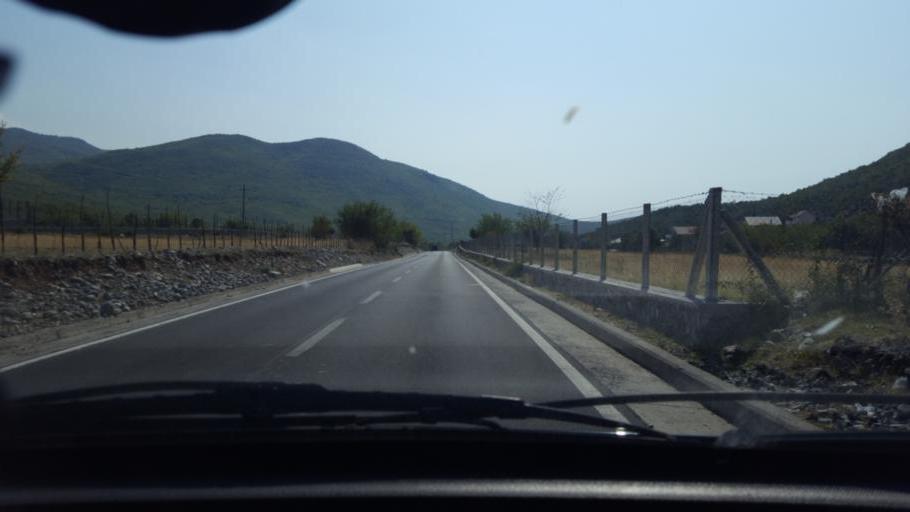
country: AL
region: Shkoder
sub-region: Rrethi i Malesia e Madhe
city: Kastrat
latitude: 42.3919
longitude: 19.4927
